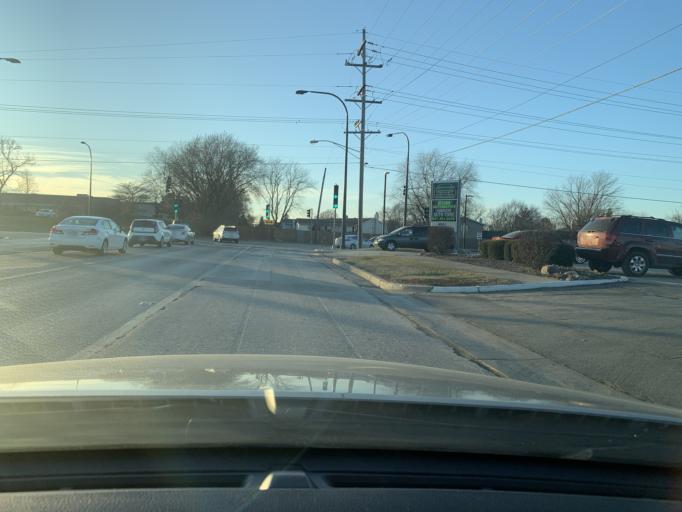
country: US
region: Illinois
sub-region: DuPage County
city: Itasca
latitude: 41.9926
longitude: -88.0307
